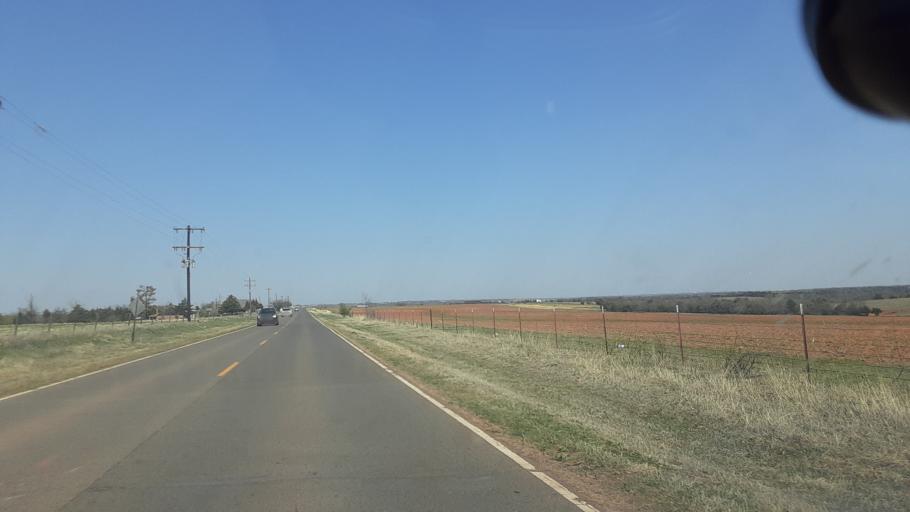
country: US
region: Oklahoma
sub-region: Logan County
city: Guthrie
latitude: 35.7844
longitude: -97.4783
